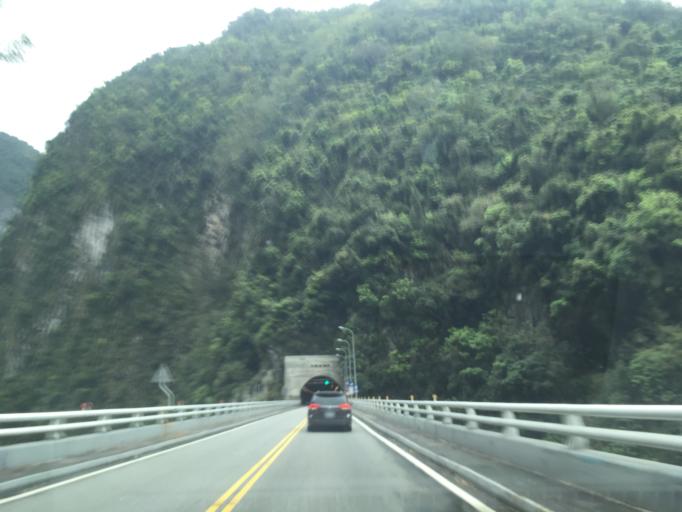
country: TW
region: Taiwan
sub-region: Hualien
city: Hualian
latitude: 24.1595
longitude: 121.6108
